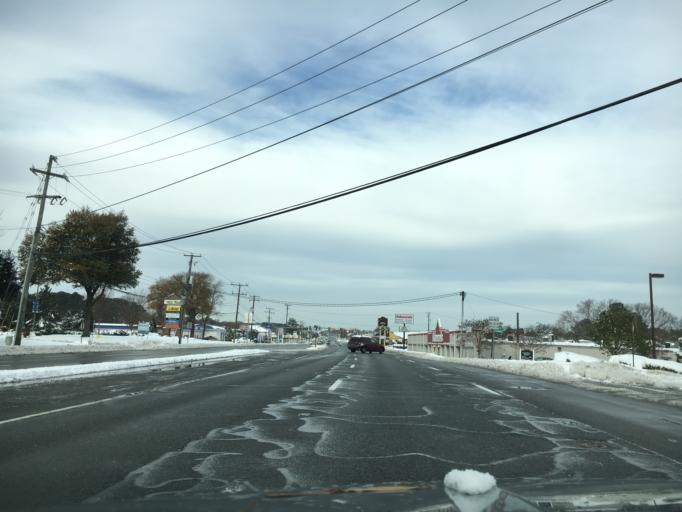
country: US
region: Virginia
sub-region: Henrico County
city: Laurel
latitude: 37.6206
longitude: -77.5249
